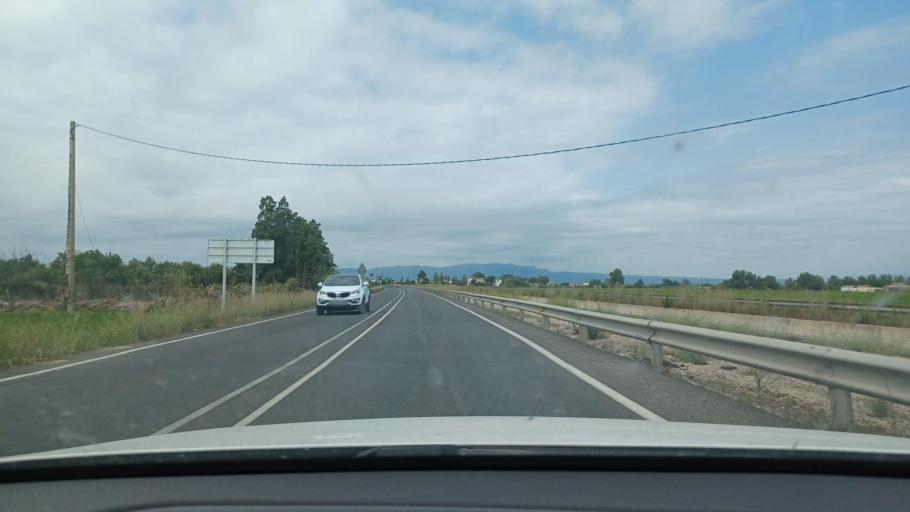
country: ES
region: Catalonia
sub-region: Provincia de Tarragona
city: Deltebre
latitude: 40.7125
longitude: 0.7559
